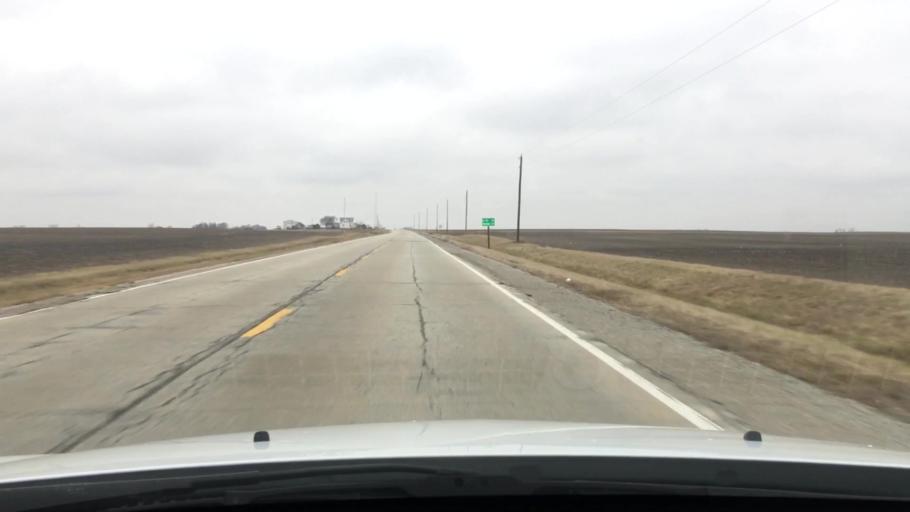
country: US
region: Illinois
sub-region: Iroquois County
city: Clifton
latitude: 40.8838
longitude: -87.9774
